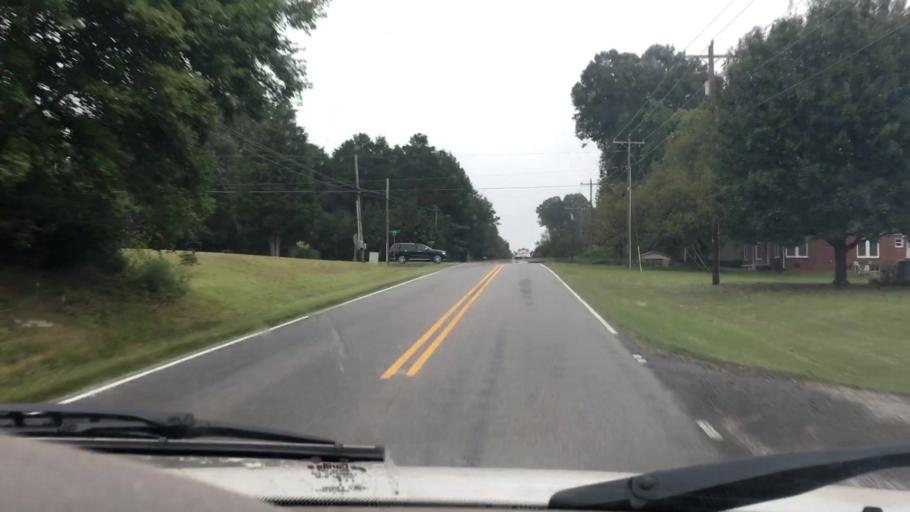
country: US
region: North Carolina
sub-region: Iredell County
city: Mooresville
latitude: 35.6120
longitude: -80.7898
